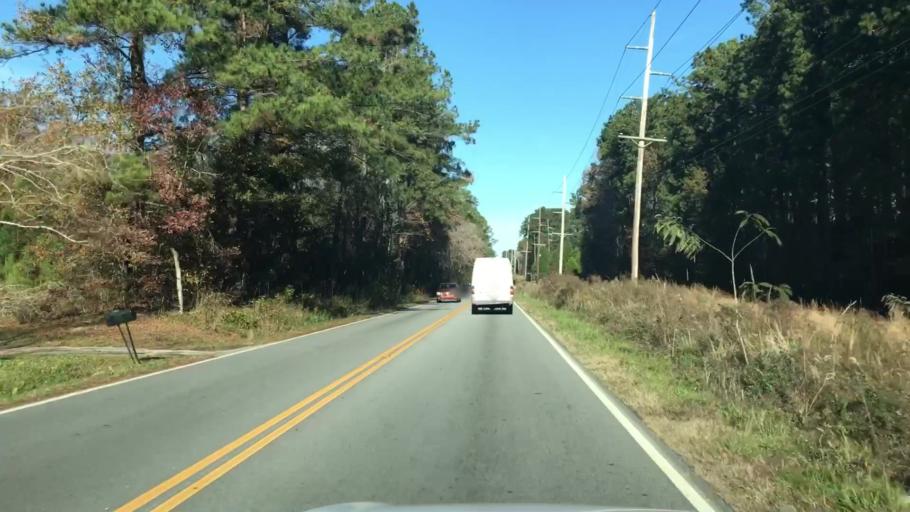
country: US
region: South Carolina
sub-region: Dorchester County
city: Centerville
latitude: 32.9840
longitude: -80.2191
